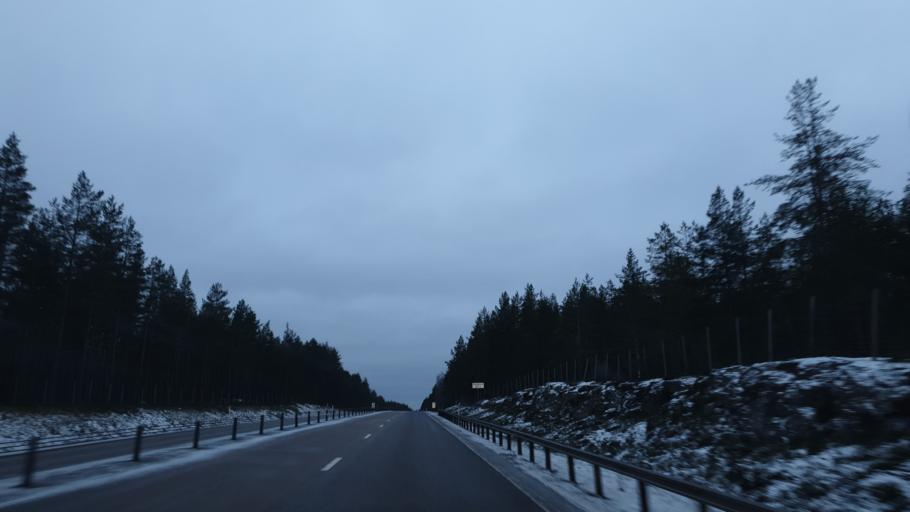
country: SE
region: Vaesterbotten
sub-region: Umea Kommun
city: Saevar
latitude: 63.9405
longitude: 20.6507
